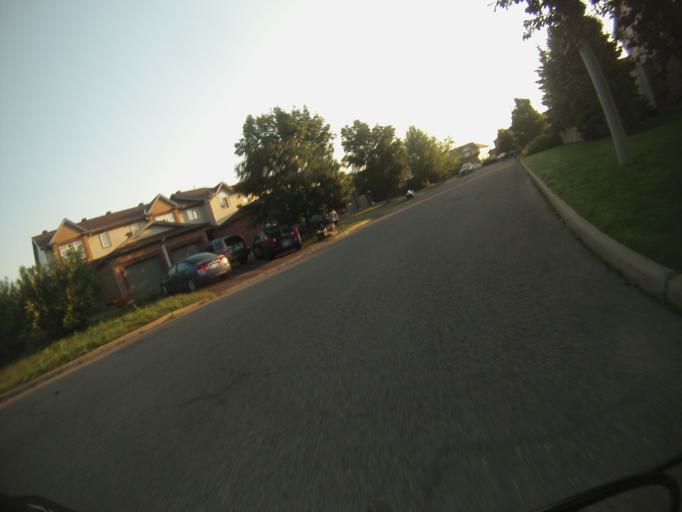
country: CA
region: Ontario
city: Ottawa
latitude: 45.3676
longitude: -75.6339
